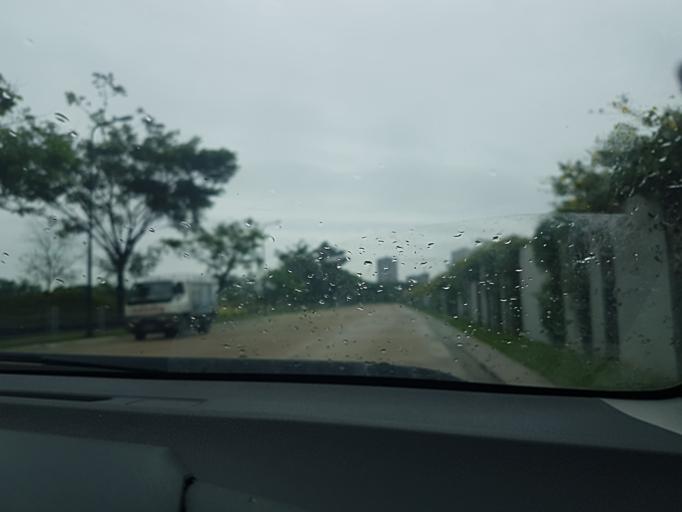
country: MM
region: Yangon
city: Syriam
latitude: 16.7784
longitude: 96.2373
